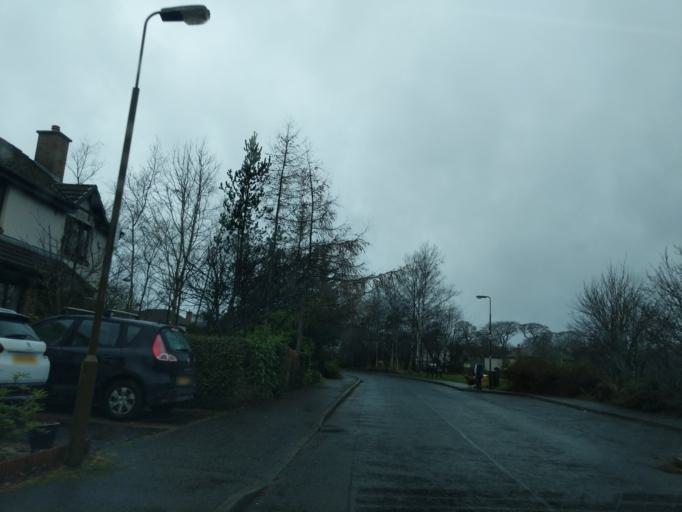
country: GB
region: Scotland
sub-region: Midlothian
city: Loanhead
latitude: 55.9065
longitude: -3.1737
